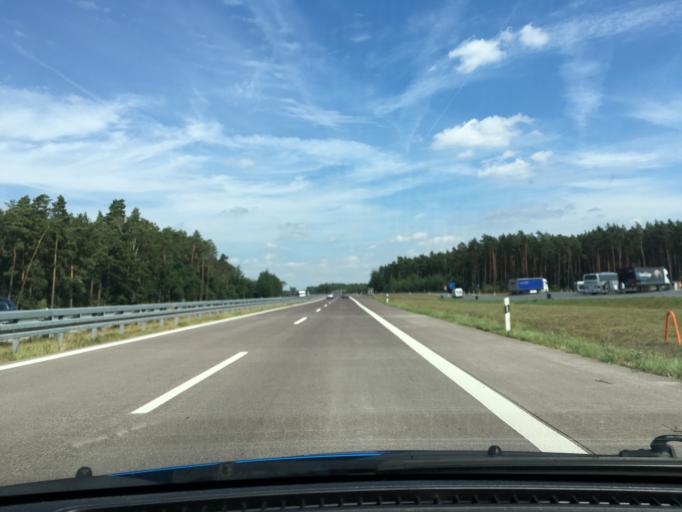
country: DE
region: Mecklenburg-Vorpommern
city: Gross Laasch
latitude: 53.3826
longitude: 11.5254
